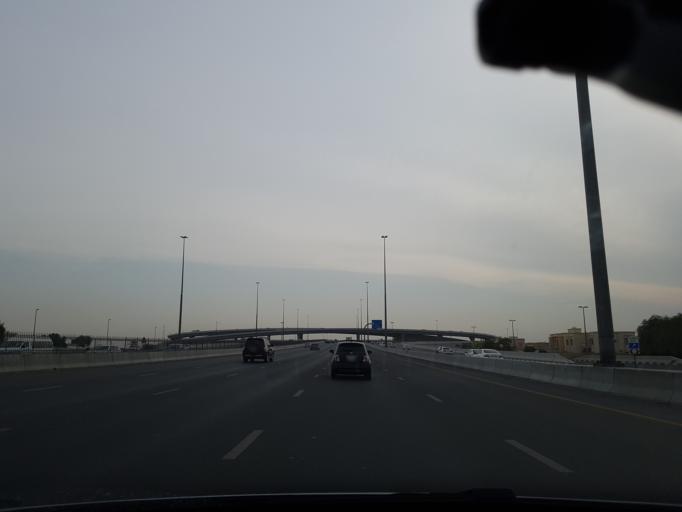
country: AE
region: Ash Shariqah
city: Sharjah
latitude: 25.3399
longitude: 55.4690
